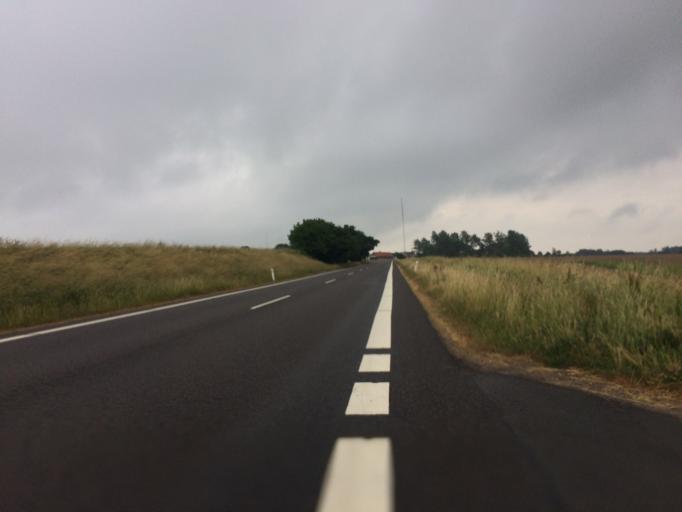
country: DK
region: Capital Region
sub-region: Bornholm Kommune
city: Akirkeby
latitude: 55.1415
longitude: 14.8630
